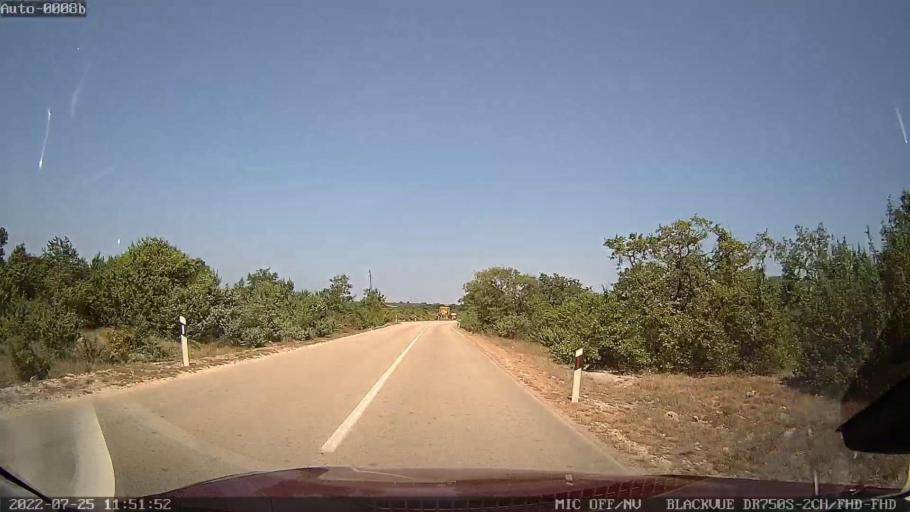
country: HR
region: Zadarska
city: Vrsi
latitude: 44.2427
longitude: 15.2486
